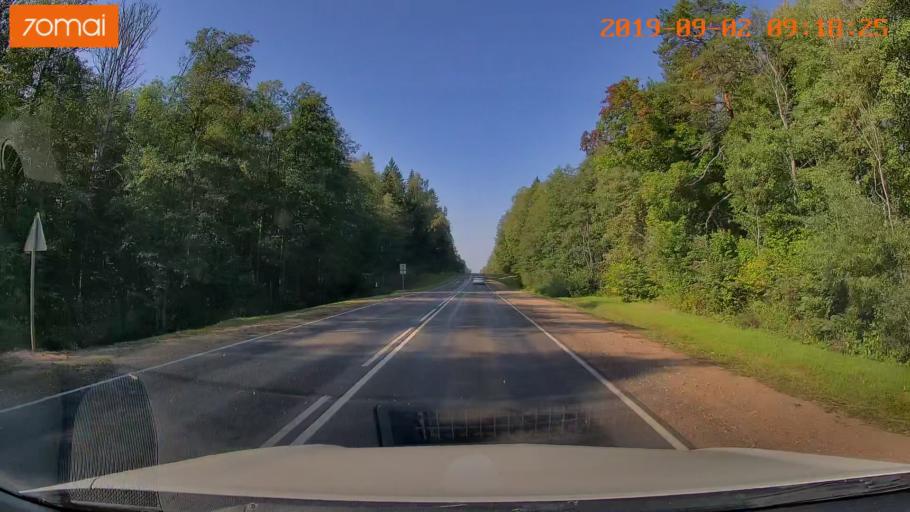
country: RU
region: Kaluga
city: Nikola-Lenivets
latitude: 54.8161
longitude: 35.4284
